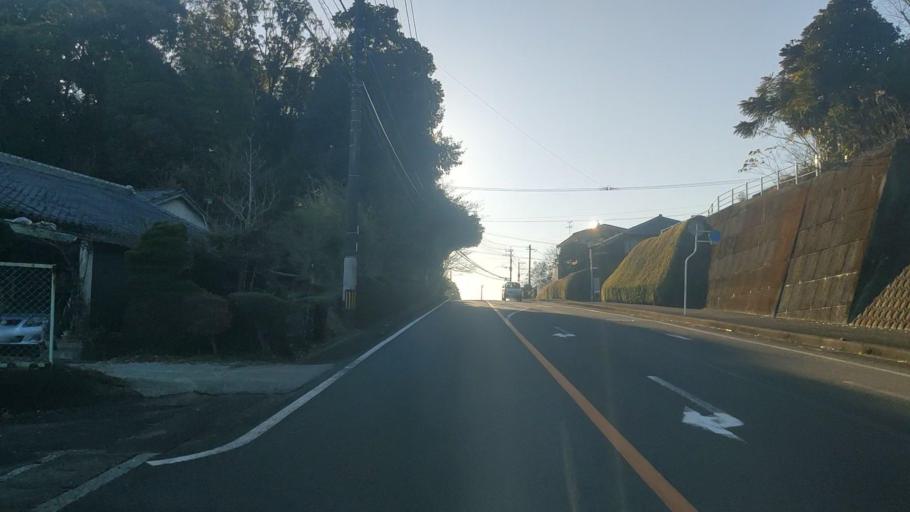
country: JP
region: Miyazaki
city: Miyazaki-shi
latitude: 31.8546
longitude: 131.3620
